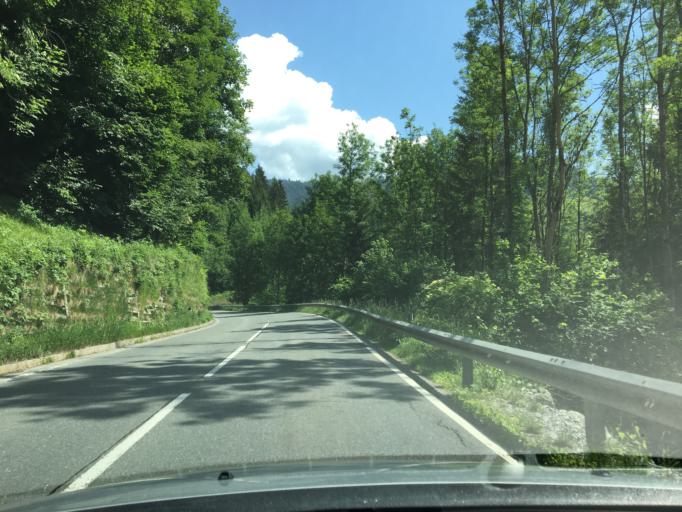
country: AT
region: Salzburg
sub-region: Politischer Bezirk Sankt Johann im Pongau
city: Sankt Johann im Pongau
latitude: 47.3424
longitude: 13.2109
